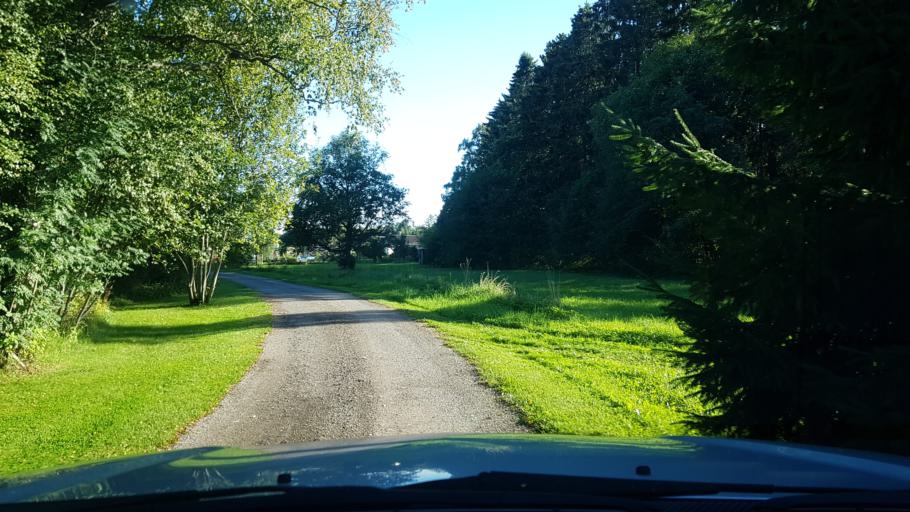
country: EE
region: Harju
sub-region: Rae vald
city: Jueri
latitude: 59.3867
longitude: 24.8685
